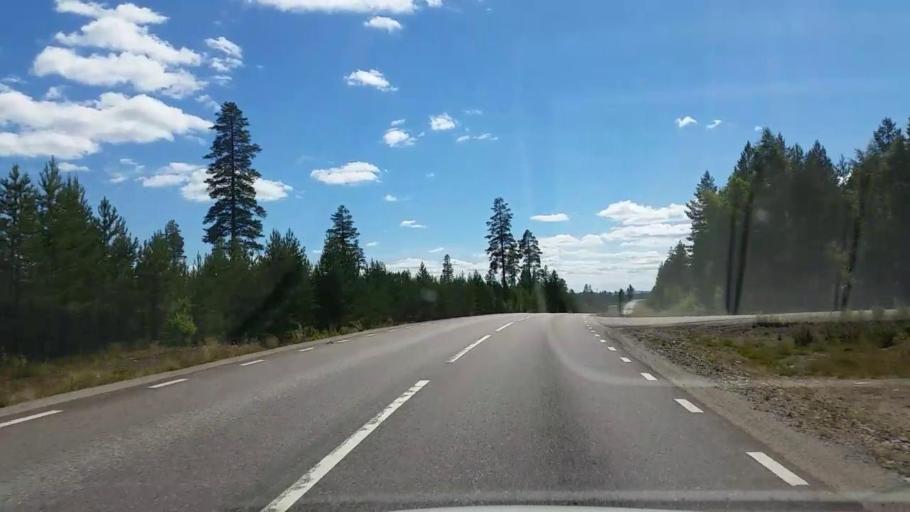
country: SE
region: Gaevleborg
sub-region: Bollnas Kommun
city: Vittsjo
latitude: 61.1092
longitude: 15.8612
